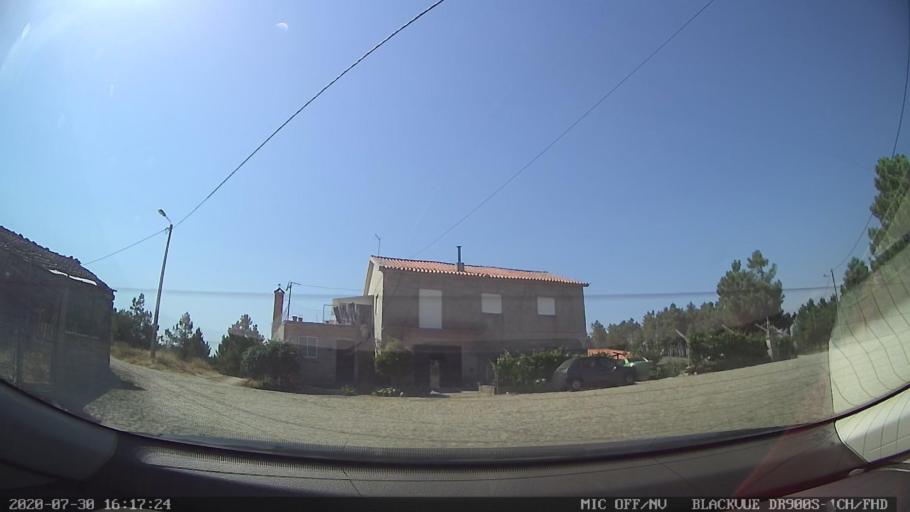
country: PT
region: Vila Real
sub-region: Murca
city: Murca
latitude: 41.3289
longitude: -7.4900
